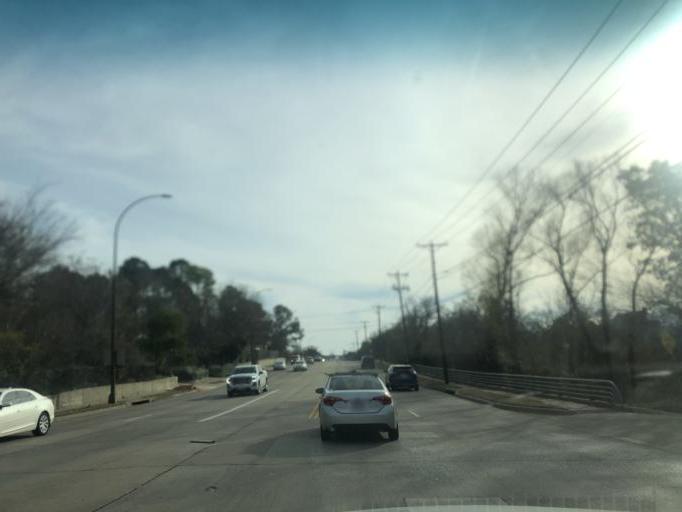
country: US
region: Texas
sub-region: Tarrant County
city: Dalworthington Gardens
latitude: 32.6833
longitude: -97.1495
